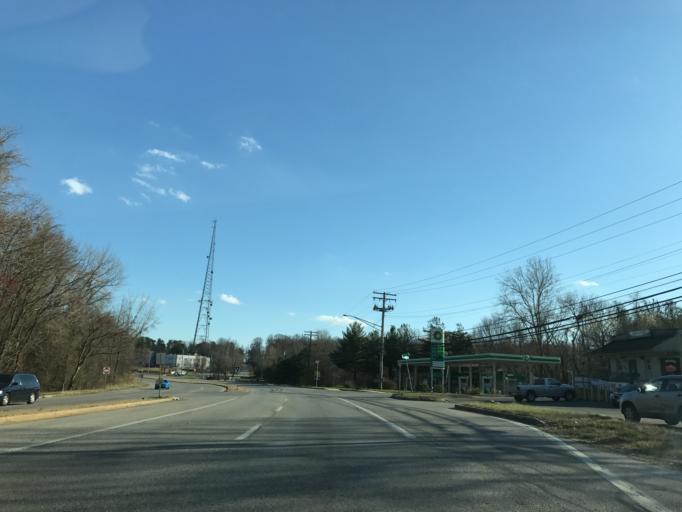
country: US
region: Maryland
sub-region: Anne Arundel County
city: Green Haven
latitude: 39.1849
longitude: -76.5518
